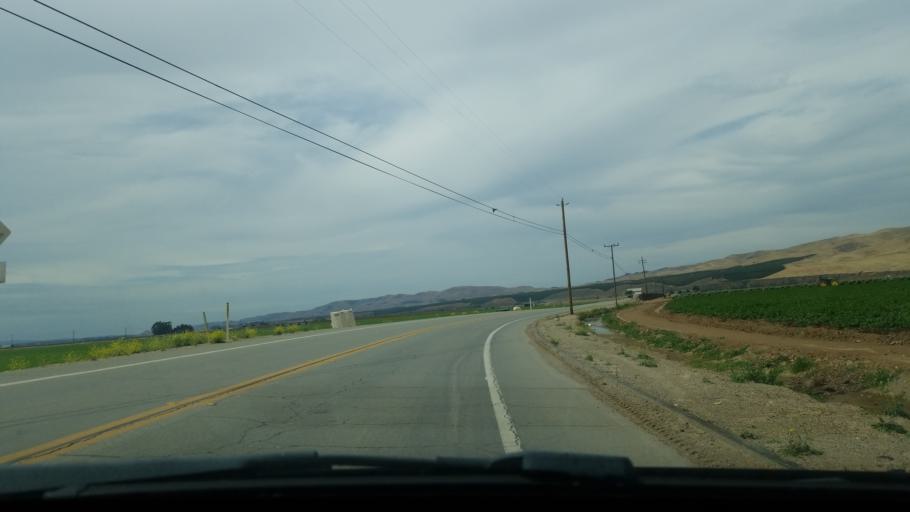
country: US
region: California
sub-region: Santa Barbara County
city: Santa Maria
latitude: 34.9113
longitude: -120.3476
